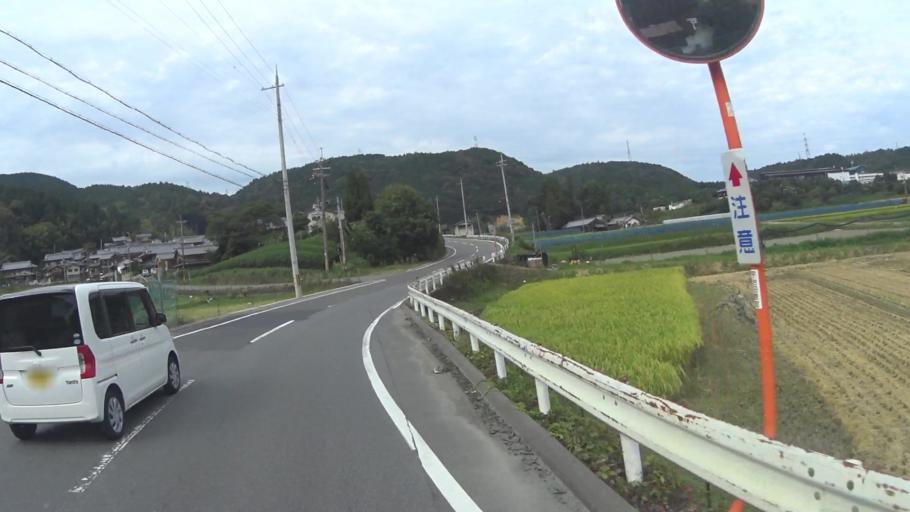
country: JP
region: Kyoto
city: Uji
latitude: 34.8724
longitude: 135.8744
